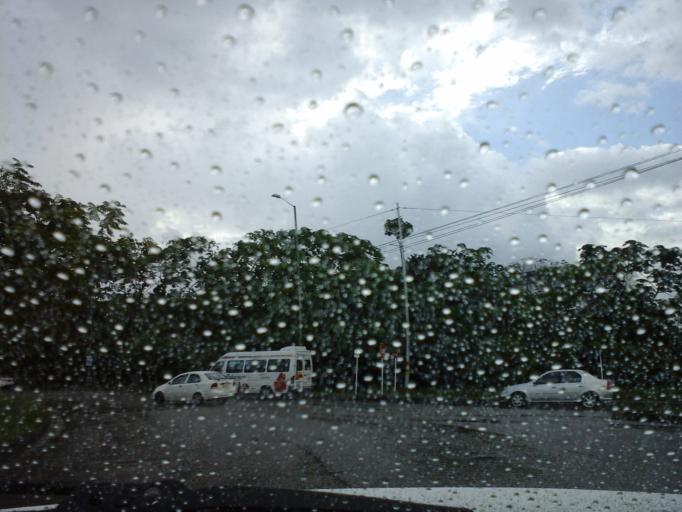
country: CO
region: Meta
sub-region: Villavicencio
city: Villavicencio
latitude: 4.1204
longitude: -73.6149
